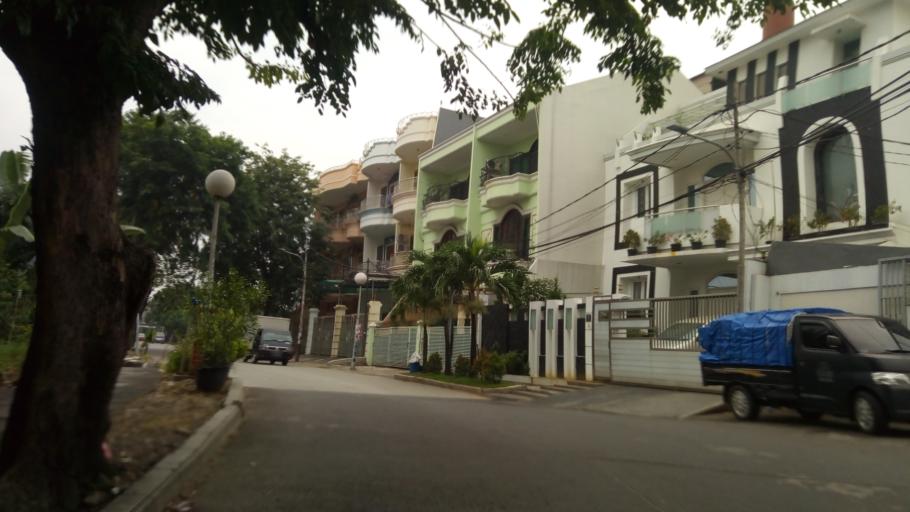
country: ID
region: Jakarta Raya
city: Jakarta
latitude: -6.1486
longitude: 106.8419
